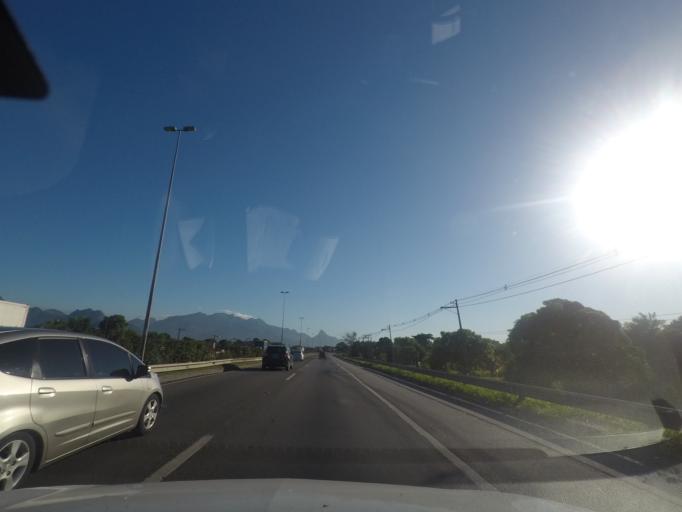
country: BR
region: Rio de Janeiro
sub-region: Duque De Caxias
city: Duque de Caxias
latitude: -22.6532
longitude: -43.2406
